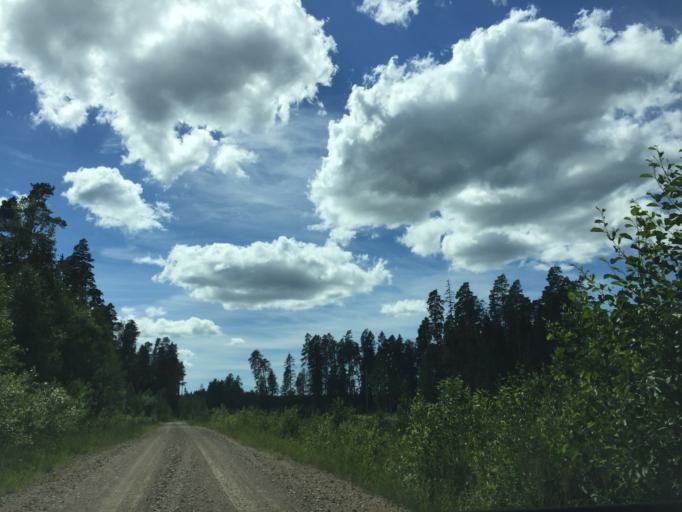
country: LV
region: Kuldigas Rajons
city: Kuldiga
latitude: 57.1043
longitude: 21.8389
